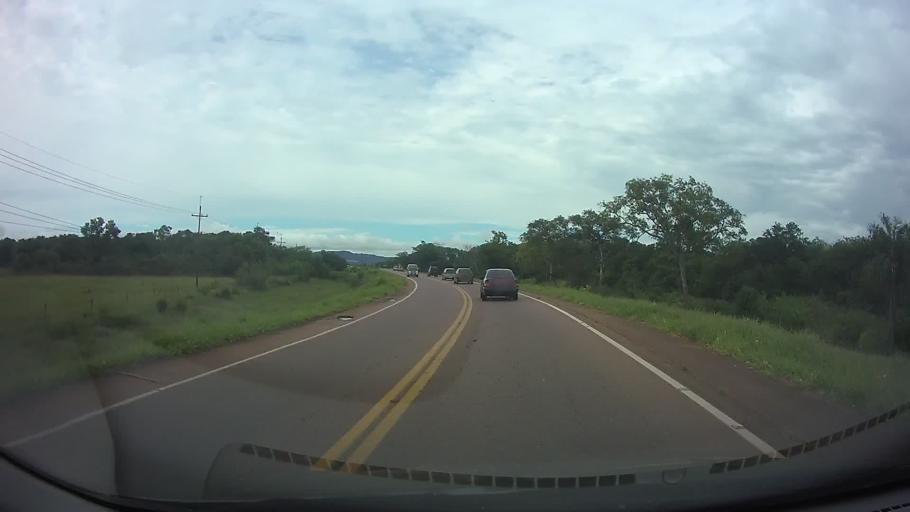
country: PY
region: Paraguari
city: Carapegua
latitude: -25.7232
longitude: -57.2039
